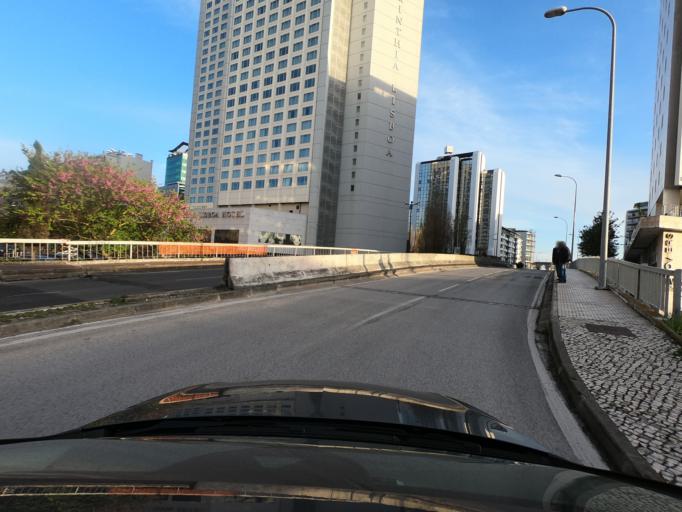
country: PT
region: Lisbon
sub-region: Lisbon
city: Lisbon
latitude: 38.7395
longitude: -9.1671
